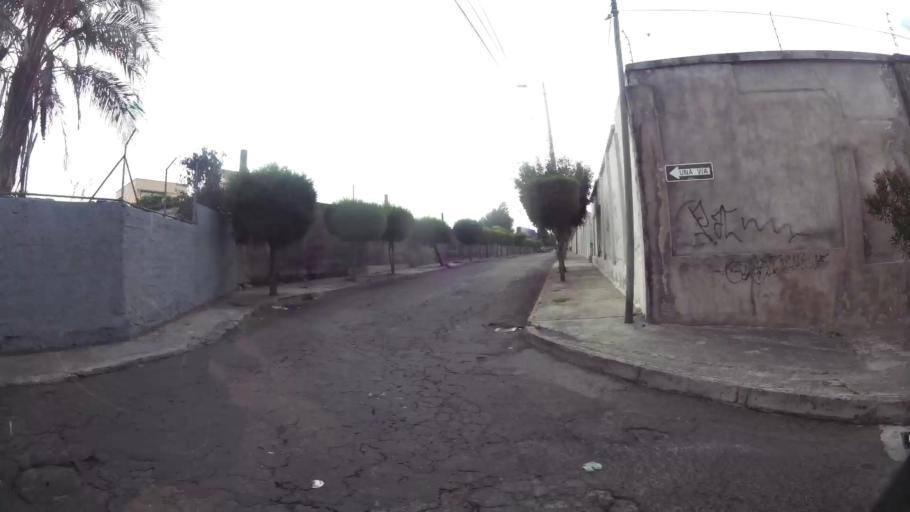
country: EC
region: Pichincha
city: Quito
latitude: -0.1593
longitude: -78.4696
